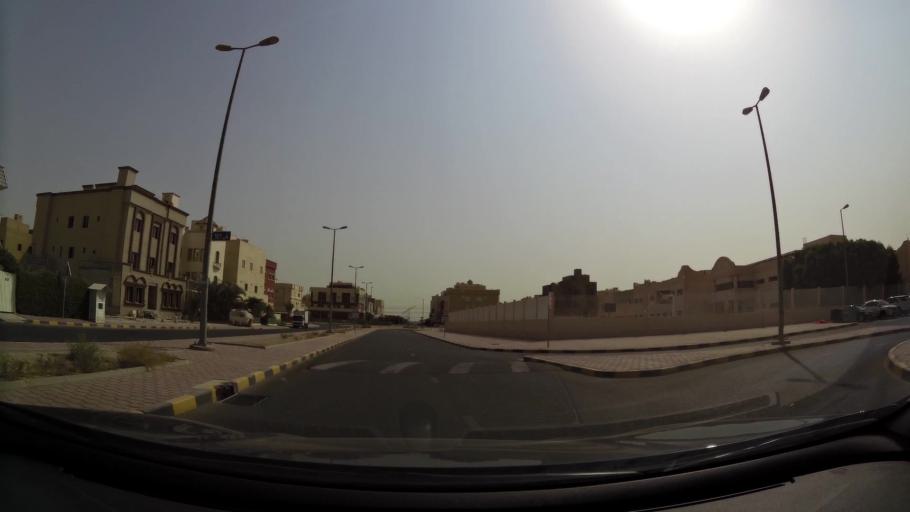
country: KW
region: Muhafazat al Jahra'
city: Al Jahra'
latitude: 29.3294
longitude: 47.7765
